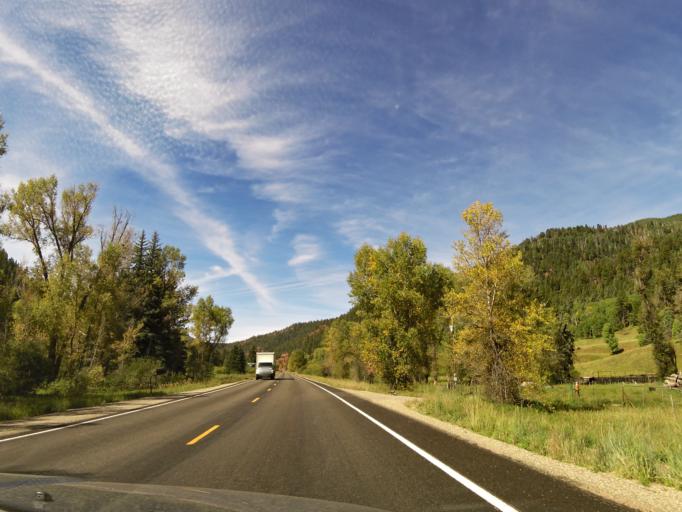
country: US
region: Colorado
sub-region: Montezuma County
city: Mancos
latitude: 37.6082
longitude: -108.0968
